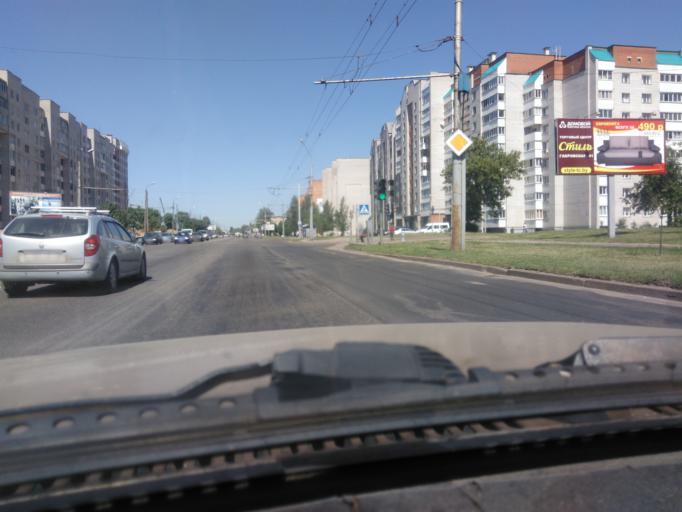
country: BY
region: Mogilev
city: Mahilyow
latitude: 53.9324
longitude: 30.3522
